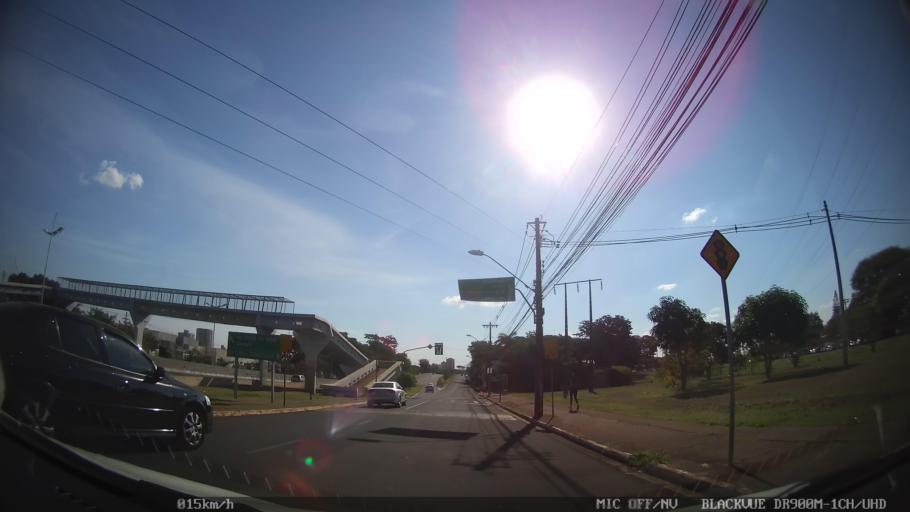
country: BR
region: Sao Paulo
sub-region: Ribeirao Preto
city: Ribeirao Preto
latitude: -21.1923
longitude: -47.7775
